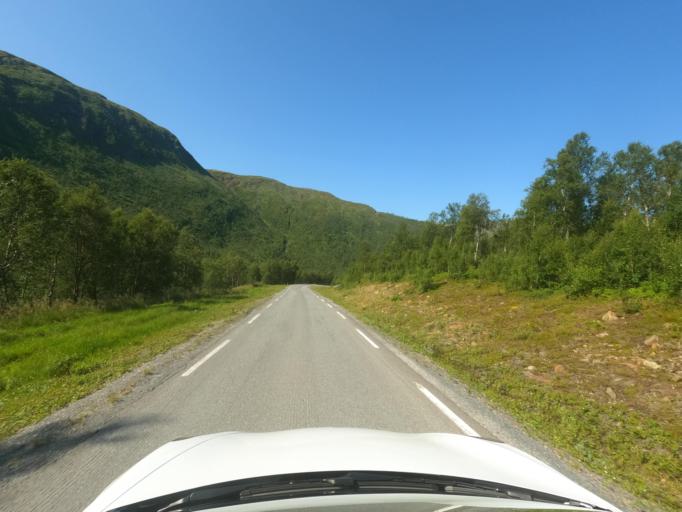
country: NO
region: Troms
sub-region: Skanland
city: Evenskjer
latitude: 68.3293
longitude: 16.5488
